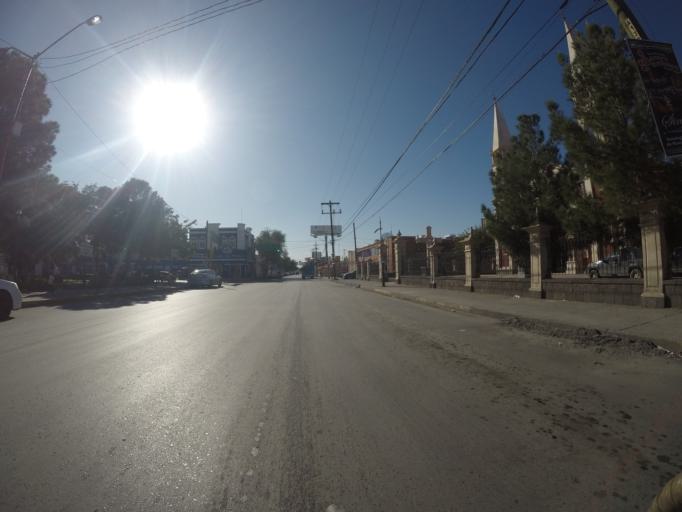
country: MX
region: Chihuahua
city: Ciudad Juarez
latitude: 31.7395
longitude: -106.4249
